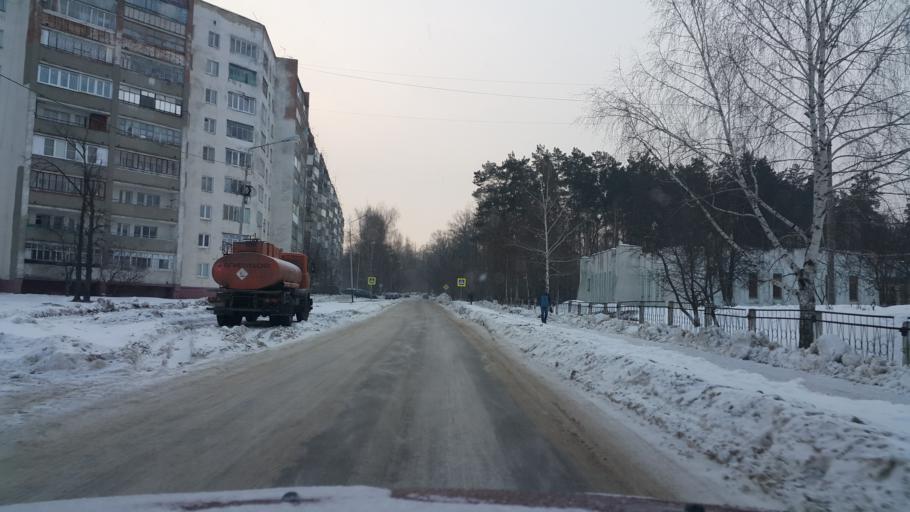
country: RU
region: Tambov
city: Kotovsk
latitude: 52.5760
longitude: 41.5158
